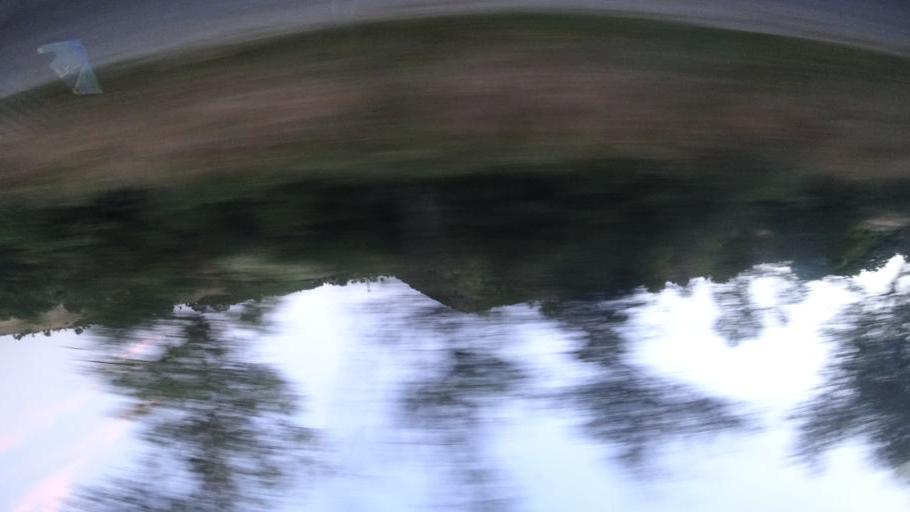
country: FR
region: Midi-Pyrenees
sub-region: Departement de l'Aveyron
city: Millau
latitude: 44.1278
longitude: 3.0539
